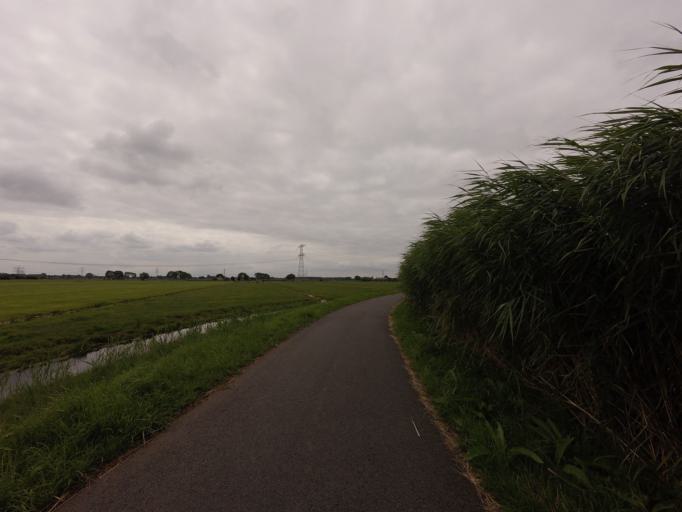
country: NL
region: South Holland
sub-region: Molenwaard
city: Nieuw-Lekkerland
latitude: 51.8769
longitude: 4.7142
